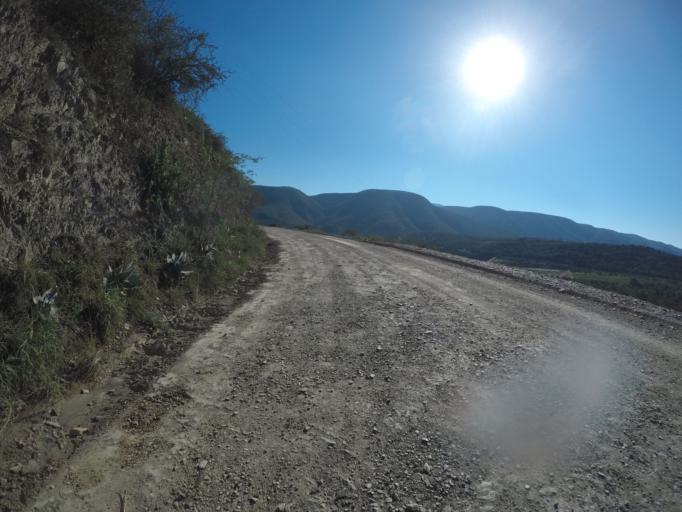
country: ZA
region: Eastern Cape
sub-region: Cacadu District Municipality
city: Kruisfontein
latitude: -33.6645
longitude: 24.5680
